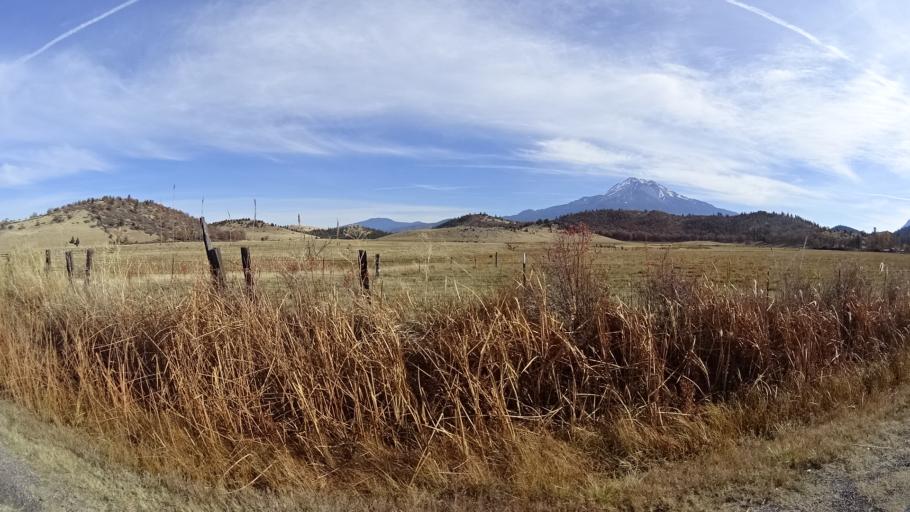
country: US
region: California
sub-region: Siskiyou County
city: Weed
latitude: 41.4635
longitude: -122.4340
